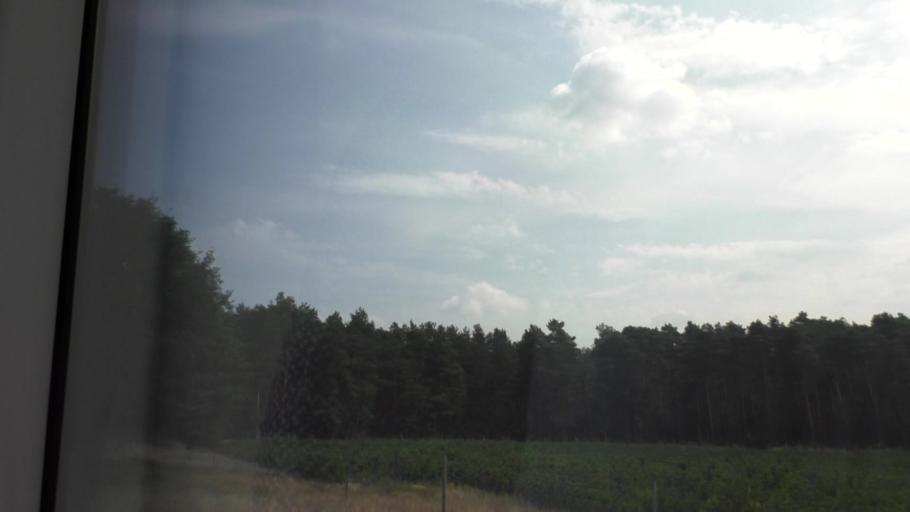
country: DE
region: Brandenburg
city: Mixdorf
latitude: 52.1624
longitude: 14.3405
